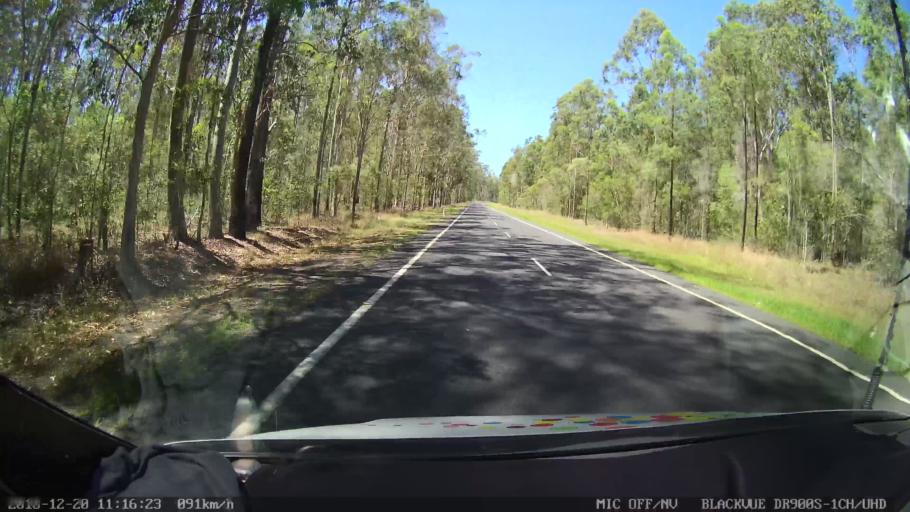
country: AU
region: New South Wales
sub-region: Richmond Valley
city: Casino
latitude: -29.0258
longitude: 153.0106
